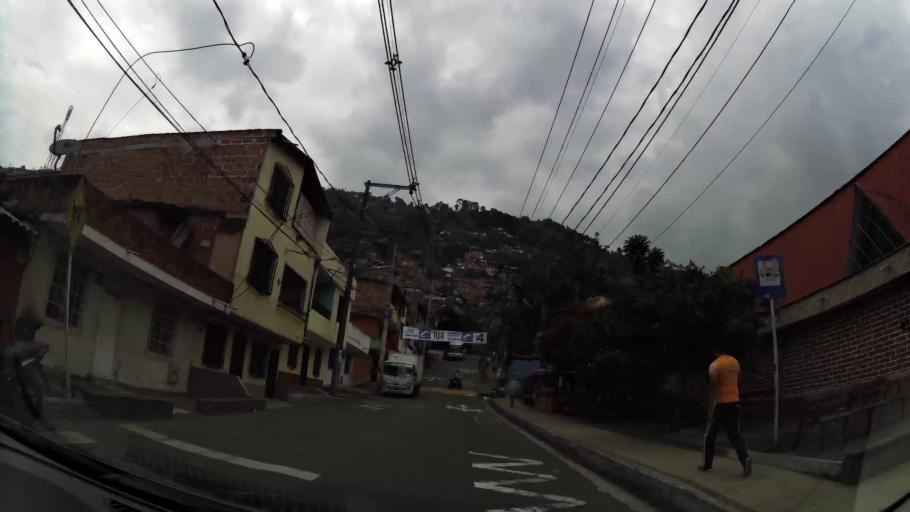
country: CO
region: Antioquia
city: Medellin
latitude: 6.2814
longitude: -75.5466
